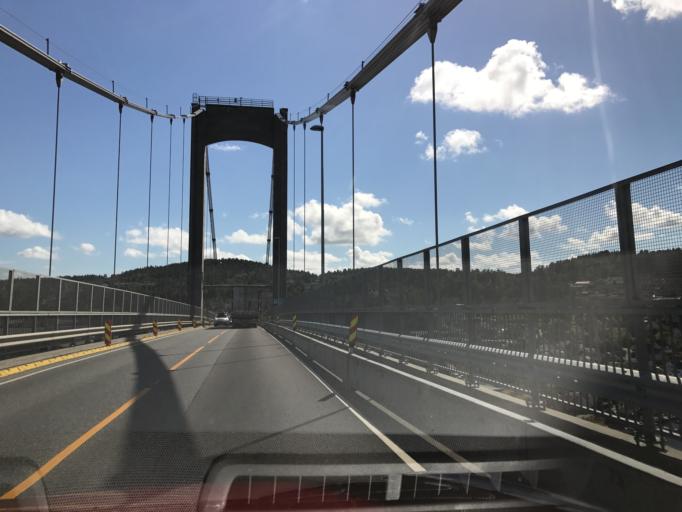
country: NO
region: Telemark
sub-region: Bamble
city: Langesund
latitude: 59.0490
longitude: 9.6941
